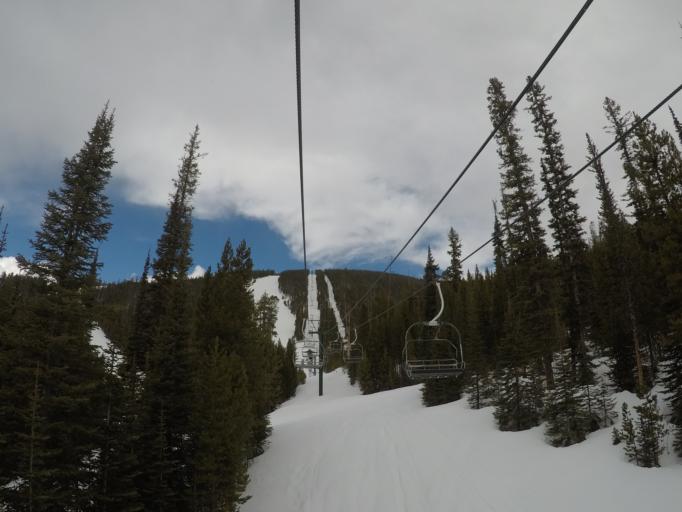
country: US
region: Montana
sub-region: Granite County
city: Philipsburg
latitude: 46.2526
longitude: -113.2419
